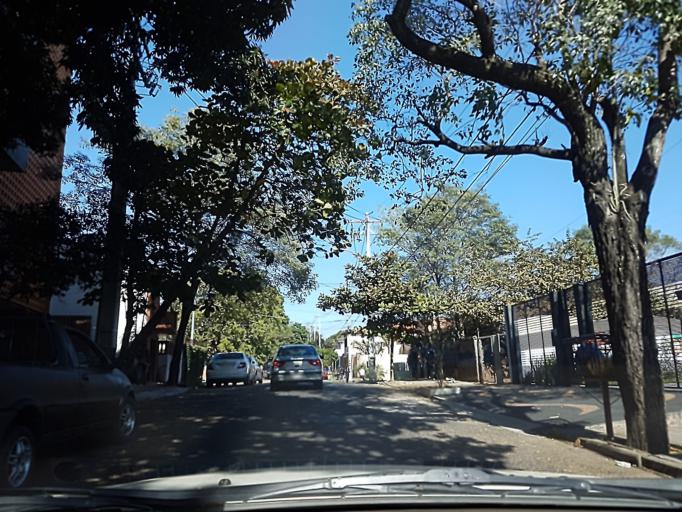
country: PY
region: Asuncion
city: Asuncion
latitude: -25.2805
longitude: -57.6039
